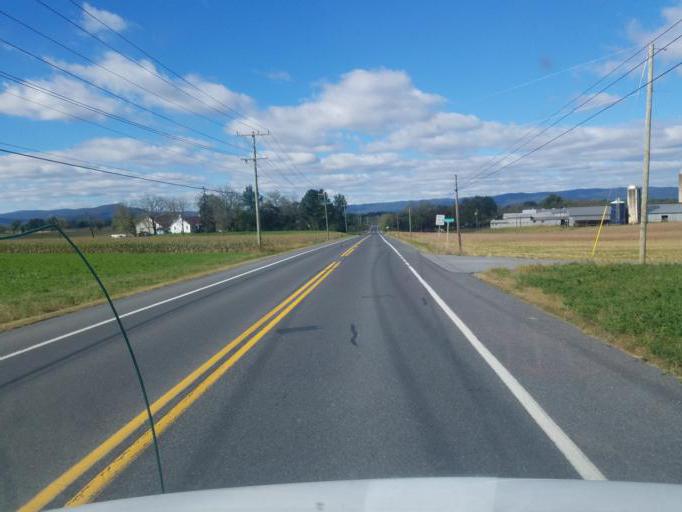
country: US
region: Pennsylvania
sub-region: Franklin County
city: Mercersburg
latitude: 39.8028
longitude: -77.8374
